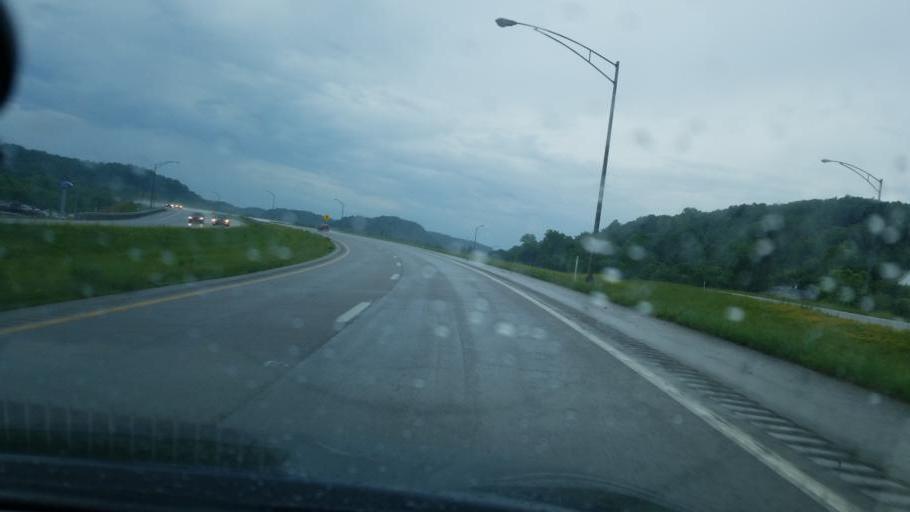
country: US
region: Ohio
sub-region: Athens County
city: Athens
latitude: 39.3355
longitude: -82.0322
